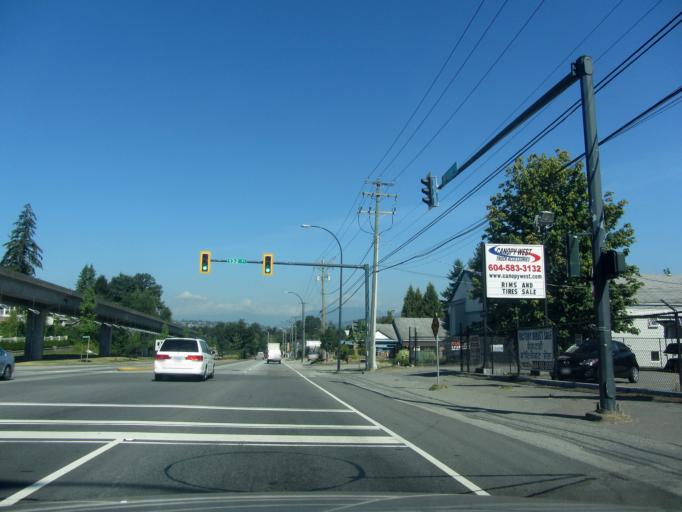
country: CA
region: British Columbia
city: New Westminster
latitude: 49.2050
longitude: -122.8543
